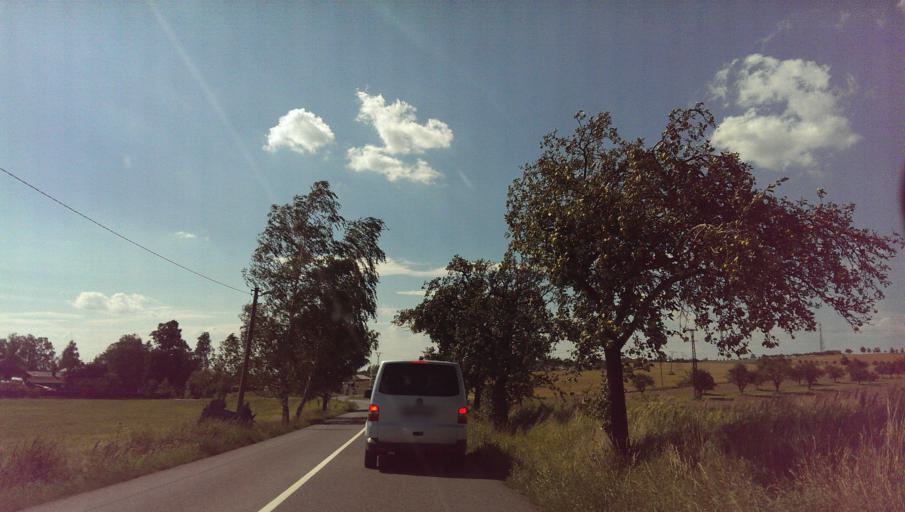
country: CZ
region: Zlin
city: Kelc
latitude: 49.4424
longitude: 17.8245
